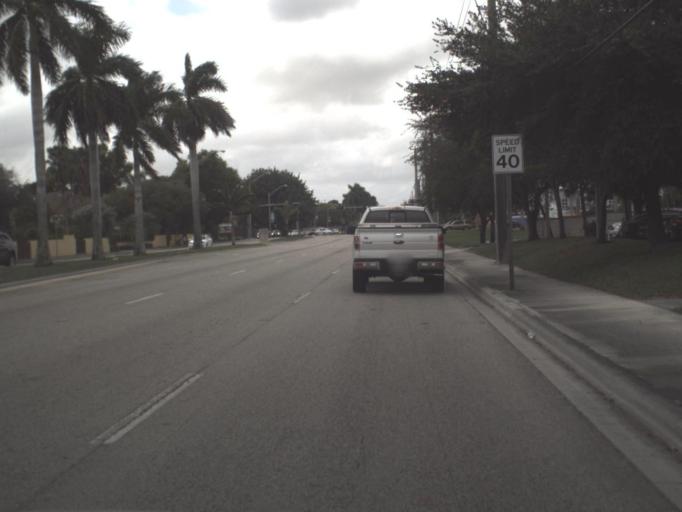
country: US
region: Florida
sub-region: Miami-Dade County
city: Doral
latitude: 25.8118
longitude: -80.3598
